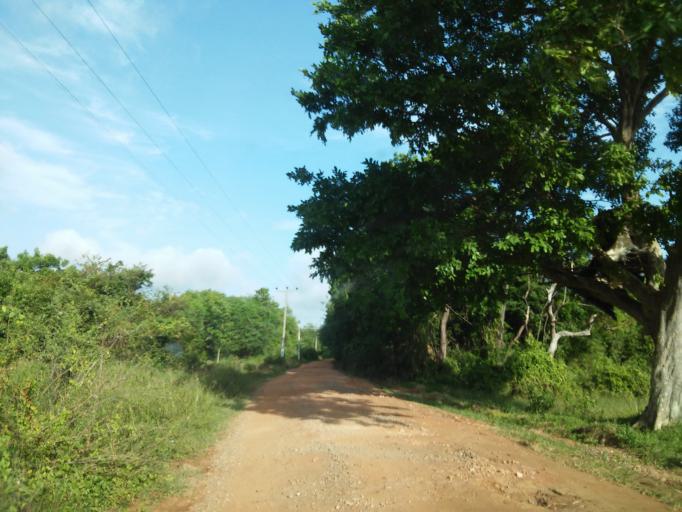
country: LK
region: Central
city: Sigiriya
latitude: 8.1717
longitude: 80.6792
